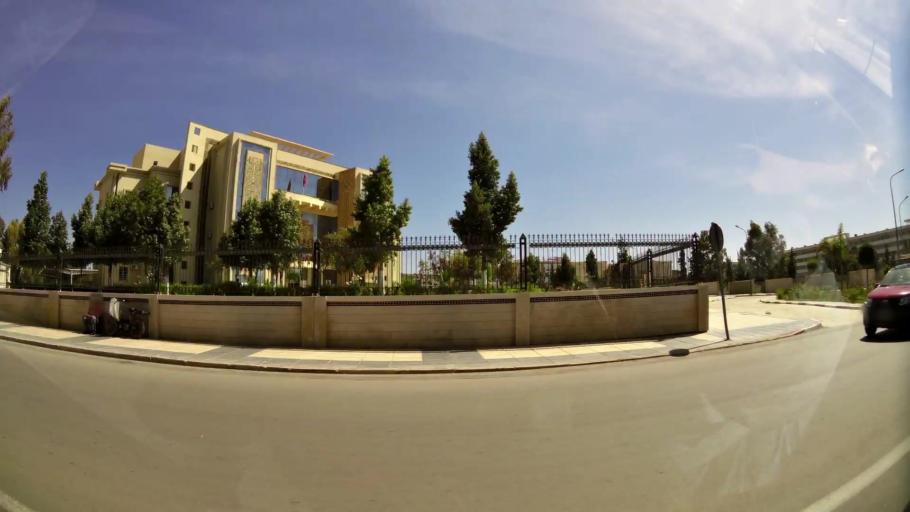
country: MA
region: Oriental
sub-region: Oujda-Angad
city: Oujda
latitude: 34.6572
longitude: -1.9082
